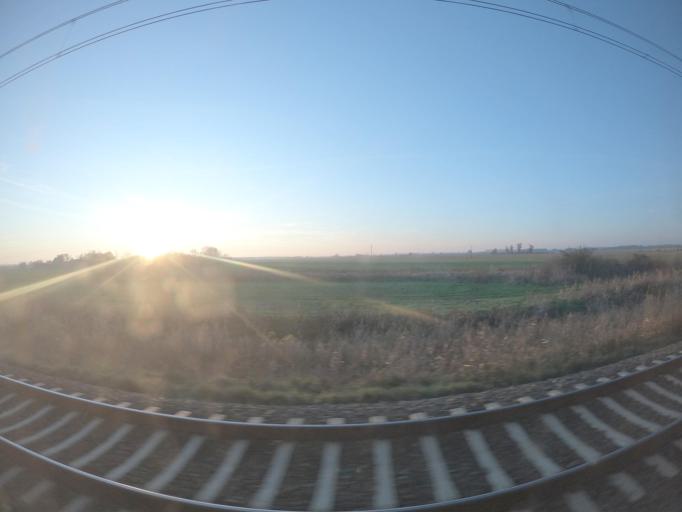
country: PL
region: Lubusz
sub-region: Powiat gorzowski
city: Kostrzyn nad Odra
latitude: 52.5449
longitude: 14.6510
